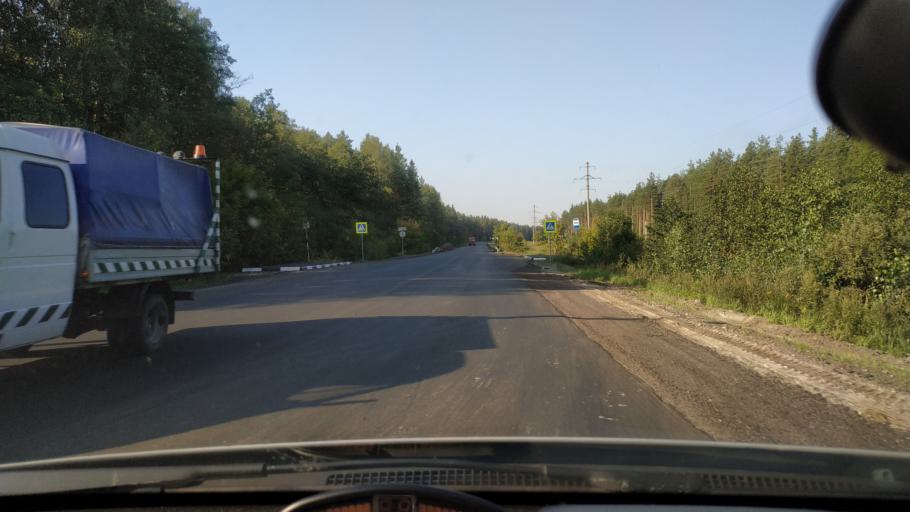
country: RU
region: Moskovskaya
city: Kerva
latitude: 55.5743
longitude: 39.6799
